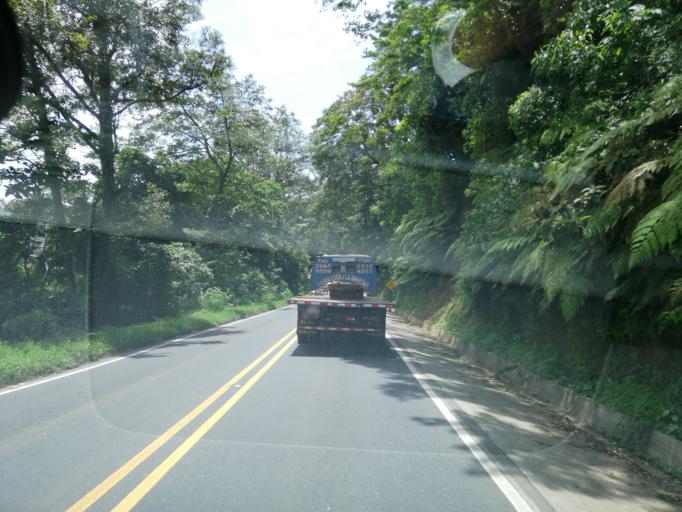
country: CR
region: Alajuela
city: Zarcero
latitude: 10.2234
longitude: -84.4082
